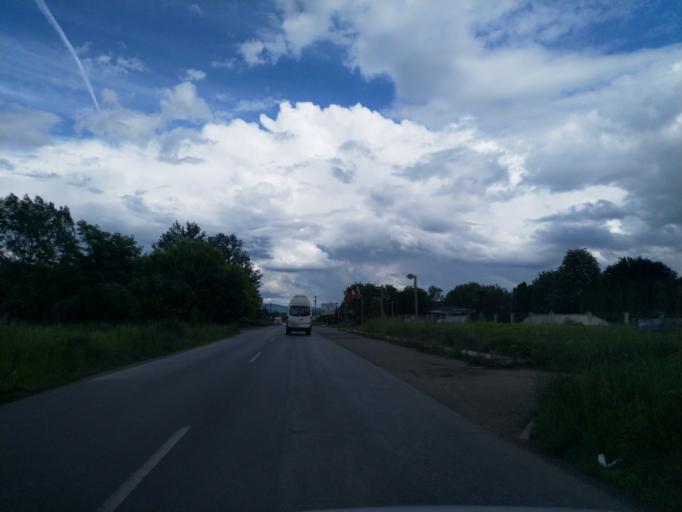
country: RS
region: Central Serbia
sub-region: Pomoravski Okrug
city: Cuprija
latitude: 43.9426
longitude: 21.3534
